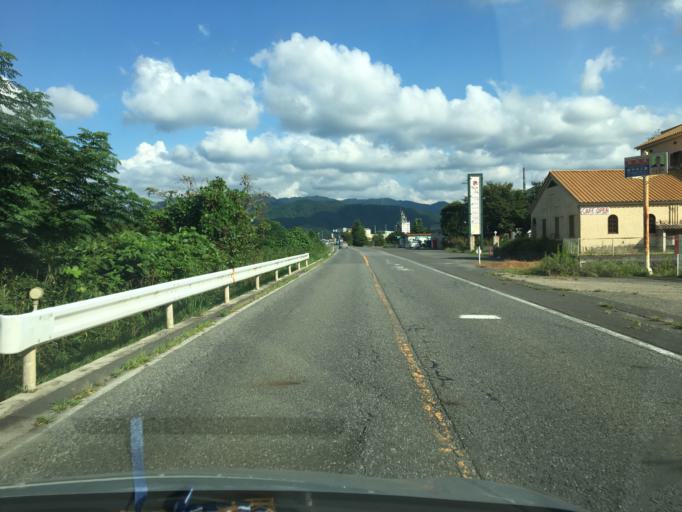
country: JP
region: Hyogo
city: Toyooka
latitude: 35.4432
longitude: 134.7769
